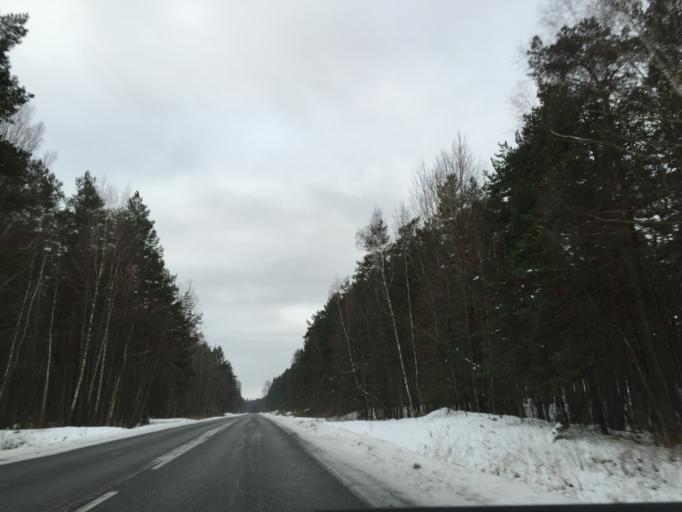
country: LV
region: Saulkrastu
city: Saulkrasti
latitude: 57.2235
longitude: 24.3900
